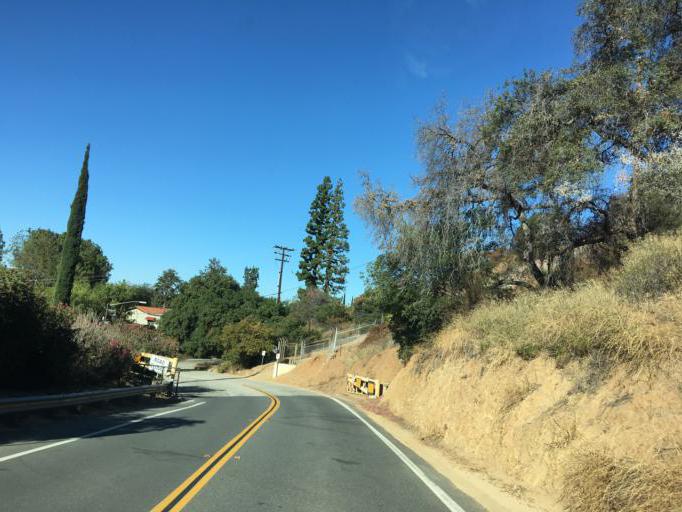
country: US
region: California
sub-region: Los Angeles County
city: Sierra Madre
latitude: 34.1719
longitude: -118.0317
